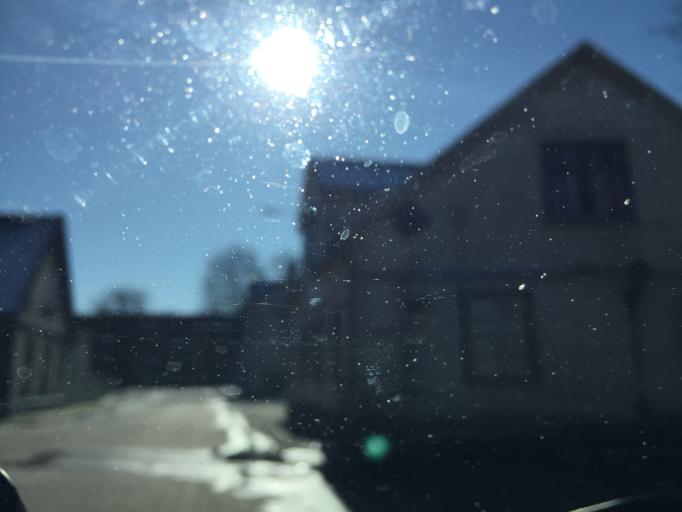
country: LV
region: Ventspils
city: Ventspils
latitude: 57.3947
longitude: 21.5620
